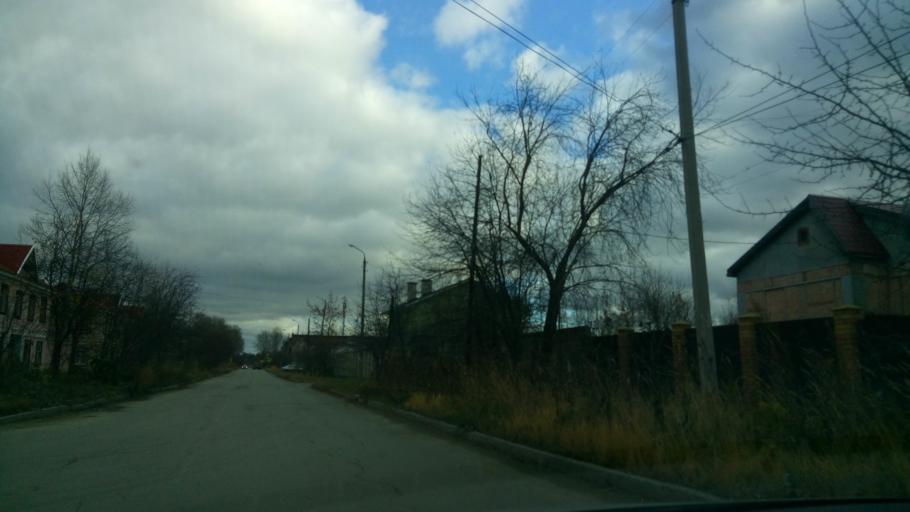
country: RU
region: Sverdlovsk
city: Sredneuralsk
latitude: 56.9843
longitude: 60.4676
